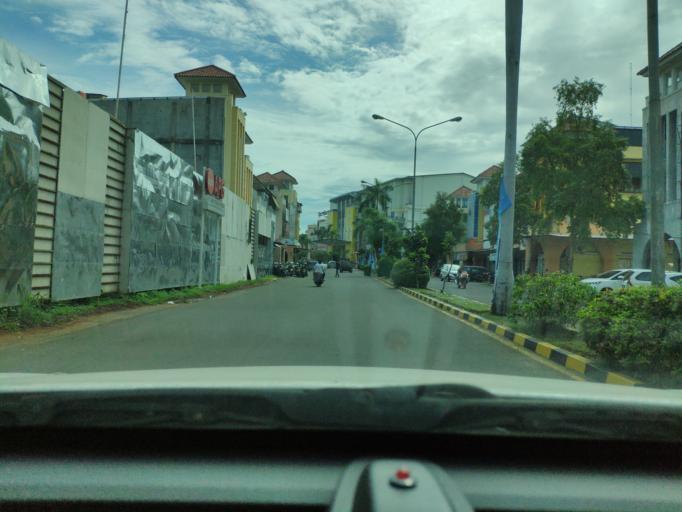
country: ID
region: West Java
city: Ciputat
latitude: -6.2219
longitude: 106.7100
